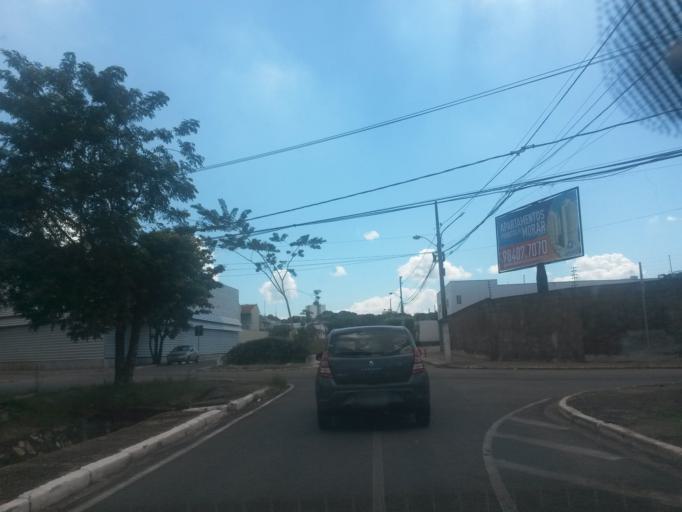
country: BR
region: Mato Grosso
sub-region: Cuiaba
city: Cuiaba
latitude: -15.6014
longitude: -56.0843
